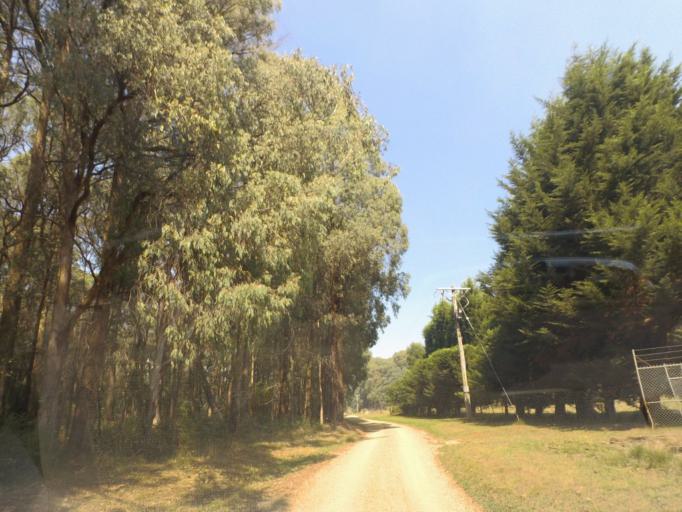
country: AU
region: Victoria
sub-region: Yarra Ranges
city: Healesville
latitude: -37.5608
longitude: 145.6449
